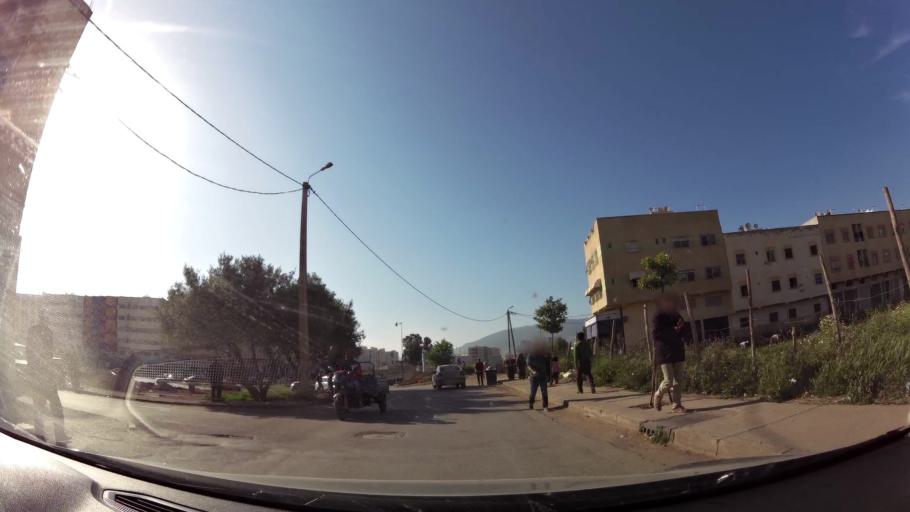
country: MA
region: Fes-Boulemane
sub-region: Fes
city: Fes
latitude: 34.0206
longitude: -5.0383
